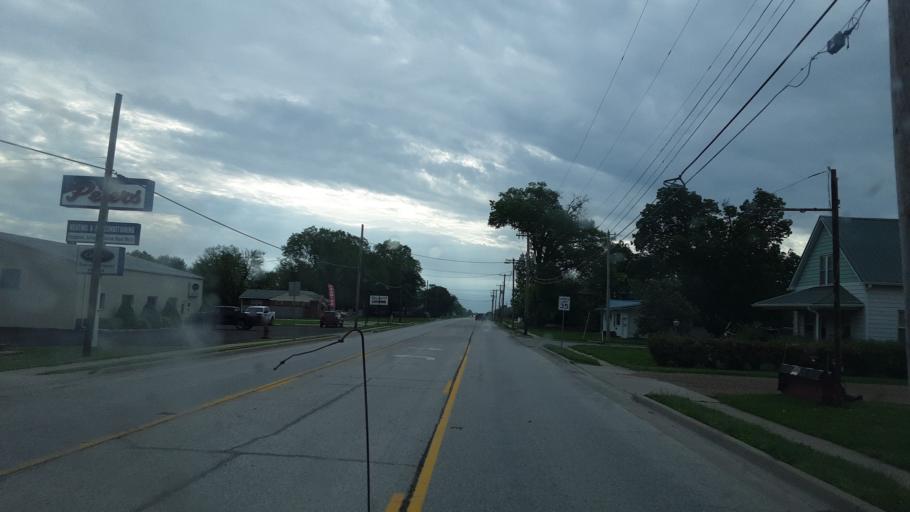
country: US
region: Illinois
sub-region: Hancock County
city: Hamilton
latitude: 40.3963
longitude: -91.3290
